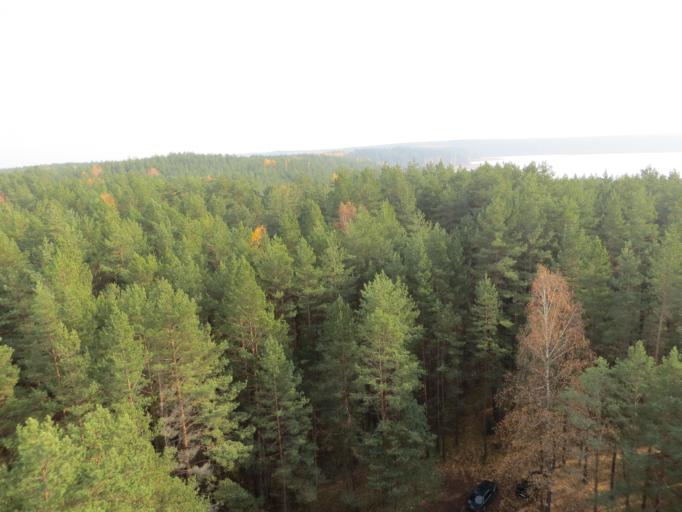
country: LT
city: Moletai
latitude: 55.2192
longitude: 25.5610
